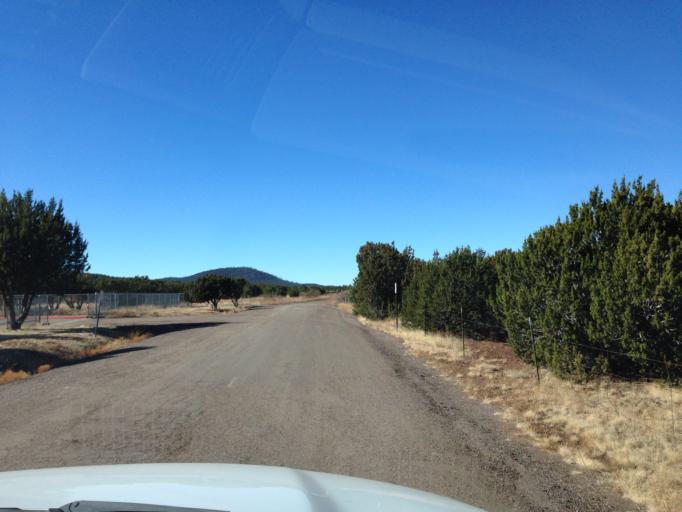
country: US
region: Arizona
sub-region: Navajo County
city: Pinetop-Lakeside
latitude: 34.2503
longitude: -109.6945
